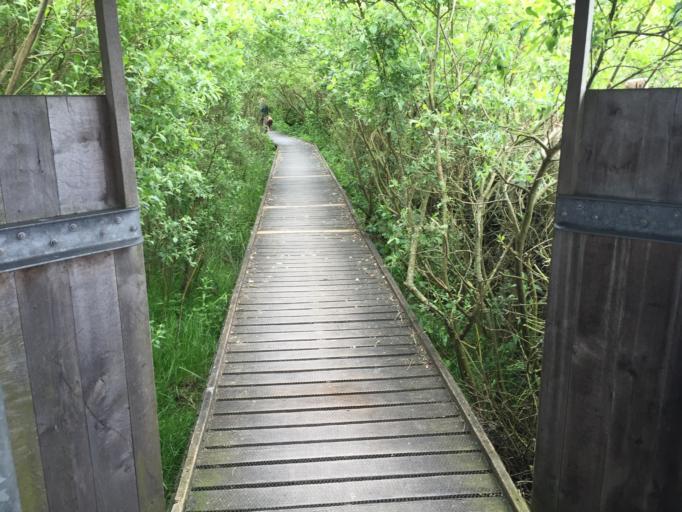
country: NL
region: Friesland
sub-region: Gemeente Schiermonnikoog
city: Schiermonnikoog
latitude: 53.4720
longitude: 6.1516
